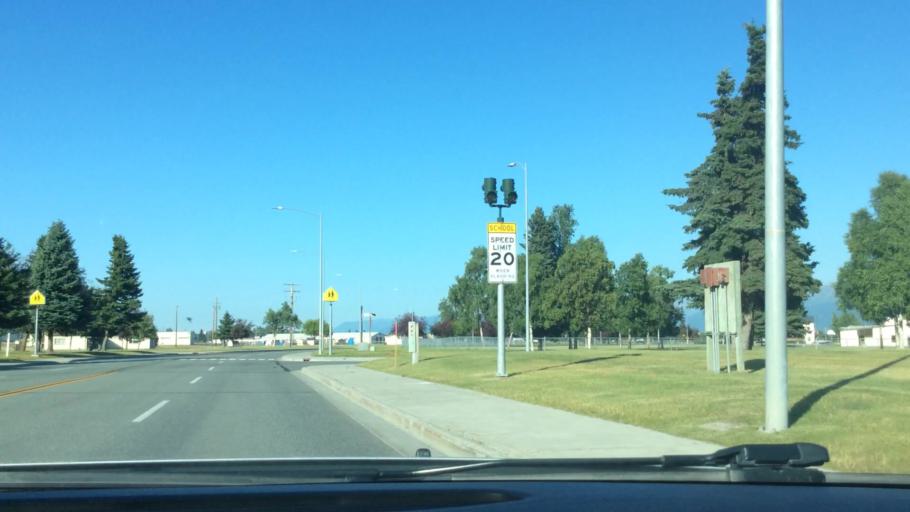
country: US
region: Alaska
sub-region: Anchorage Municipality
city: Anchorage
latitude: 61.2343
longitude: -149.8654
